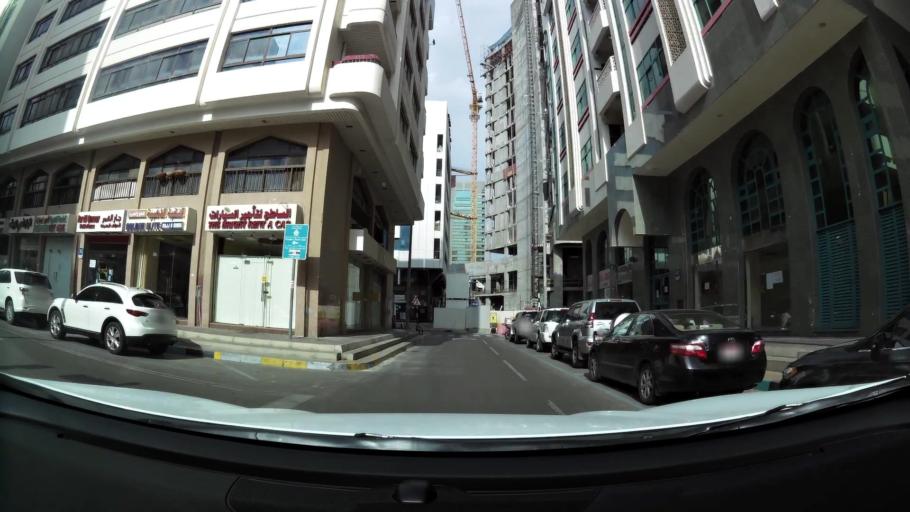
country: AE
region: Abu Dhabi
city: Abu Dhabi
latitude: 24.4711
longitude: 54.3492
